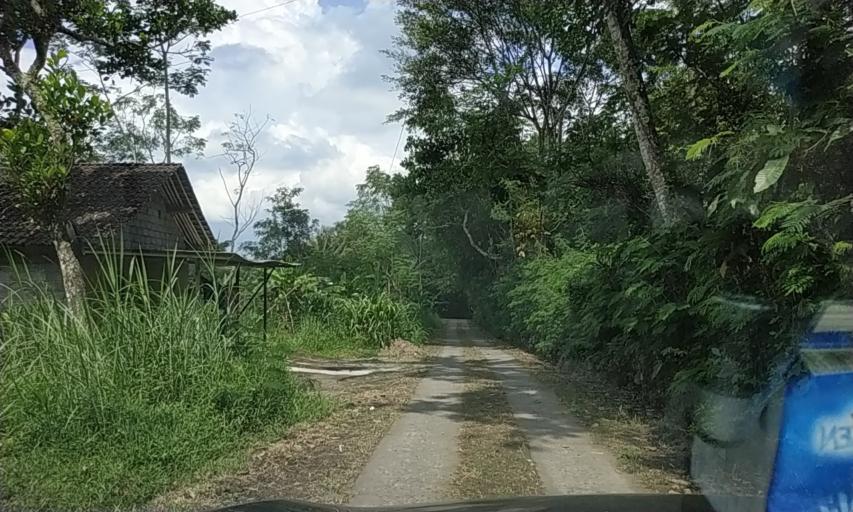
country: ID
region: Central Java
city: Jogonalan
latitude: -7.6326
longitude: 110.4849
